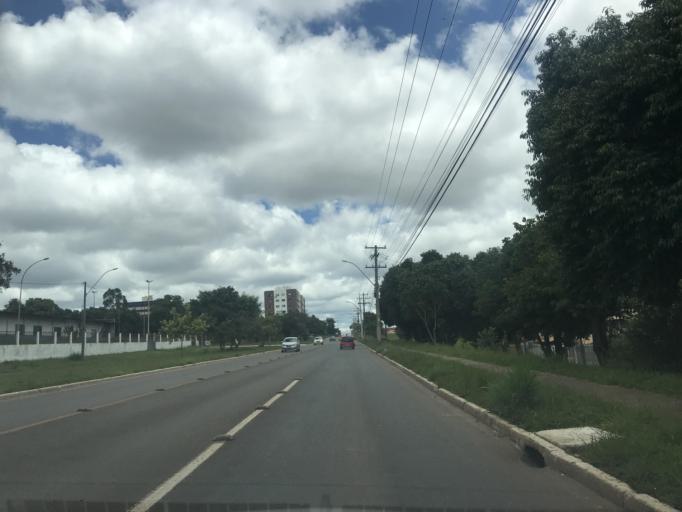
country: BR
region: Federal District
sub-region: Brasilia
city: Brasilia
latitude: -15.6540
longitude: -47.7932
